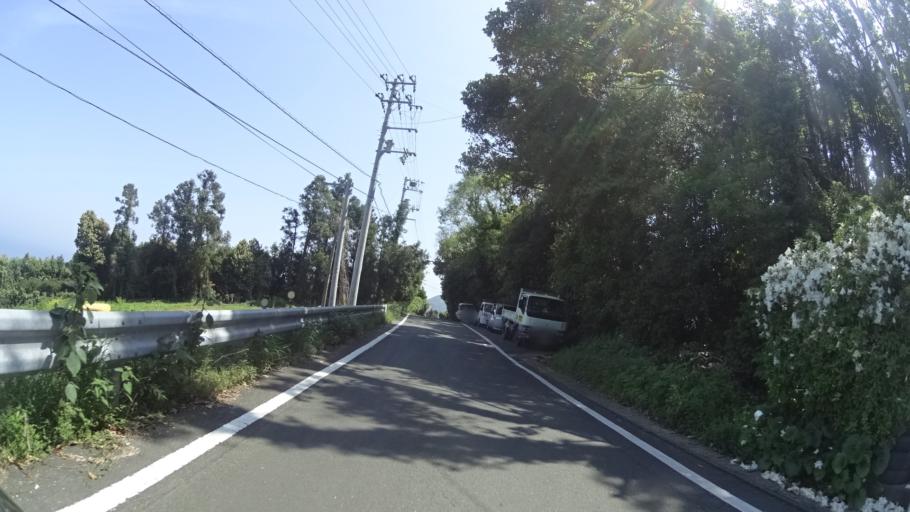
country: JP
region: Ehime
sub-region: Nishiuwa-gun
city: Ikata-cho
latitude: 33.3807
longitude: 132.0699
